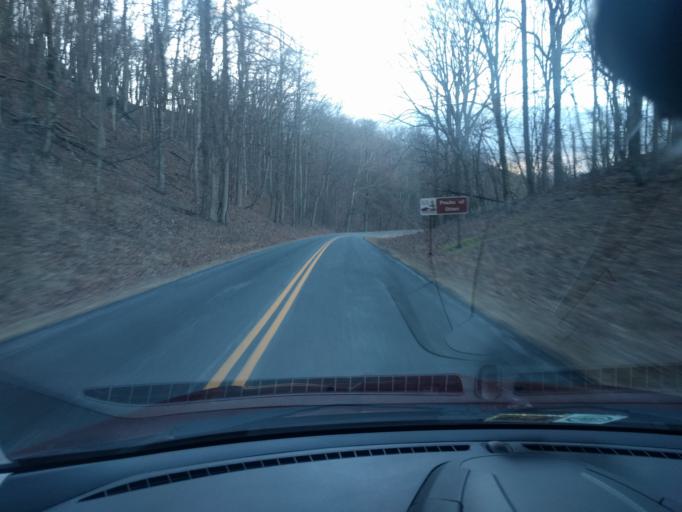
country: US
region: Virginia
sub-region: Botetourt County
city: Buchanan
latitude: 37.4474
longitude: -79.6186
